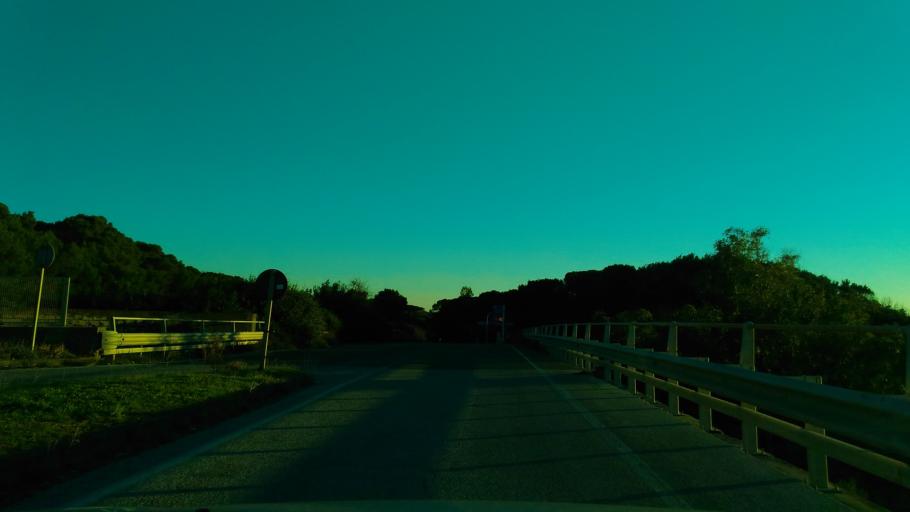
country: IT
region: Tuscany
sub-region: Provincia di Livorno
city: Quercianella
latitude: 43.4454
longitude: 10.3828
